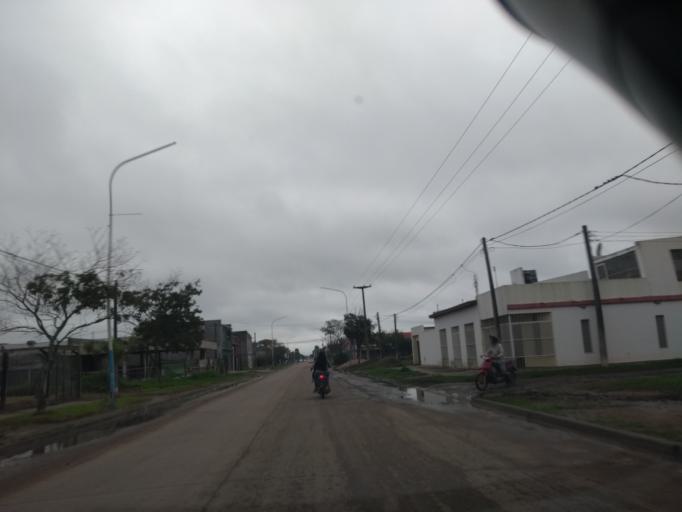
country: AR
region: Chaco
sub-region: Departamento de Quitilipi
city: Quitilipi
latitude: -26.8791
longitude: -60.2208
